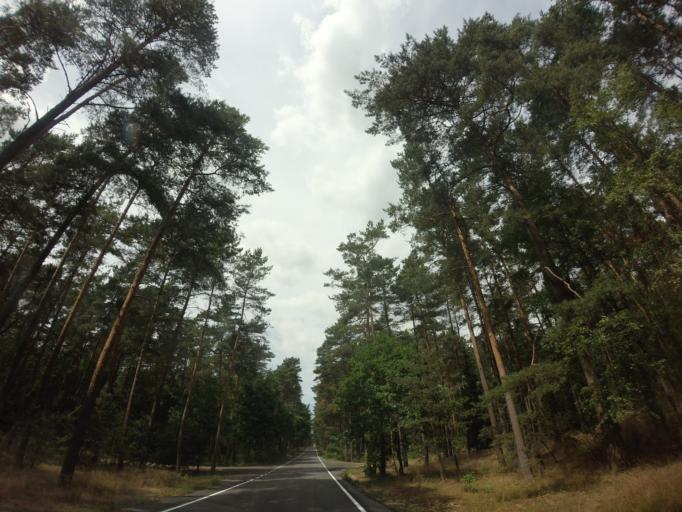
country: PL
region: West Pomeranian Voivodeship
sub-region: Powiat choszczenski
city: Drawno
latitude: 53.1361
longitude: 15.7157
